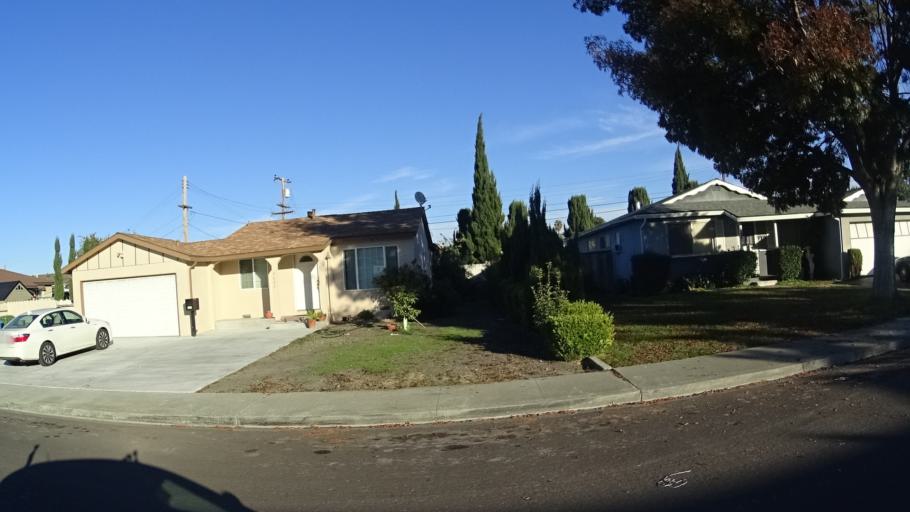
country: US
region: California
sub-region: Santa Clara County
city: Santa Clara
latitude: 37.3694
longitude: -121.9896
